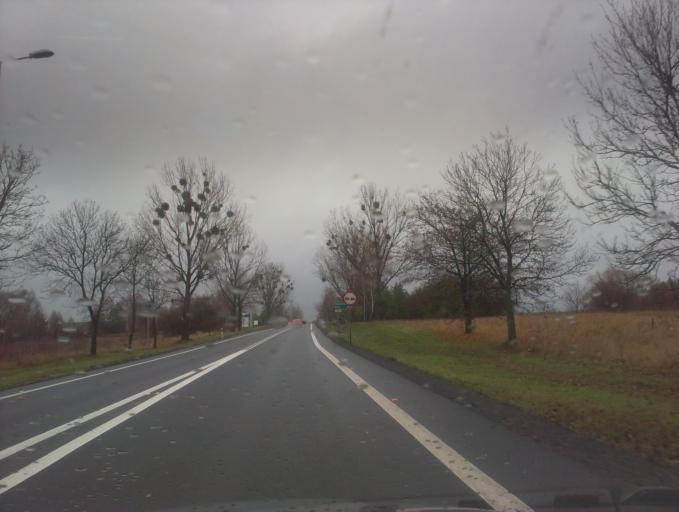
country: PL
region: Greater Poland Voivodeship
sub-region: Powiat poznanski
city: Zlotniki
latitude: 52.5366
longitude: 16.8363
